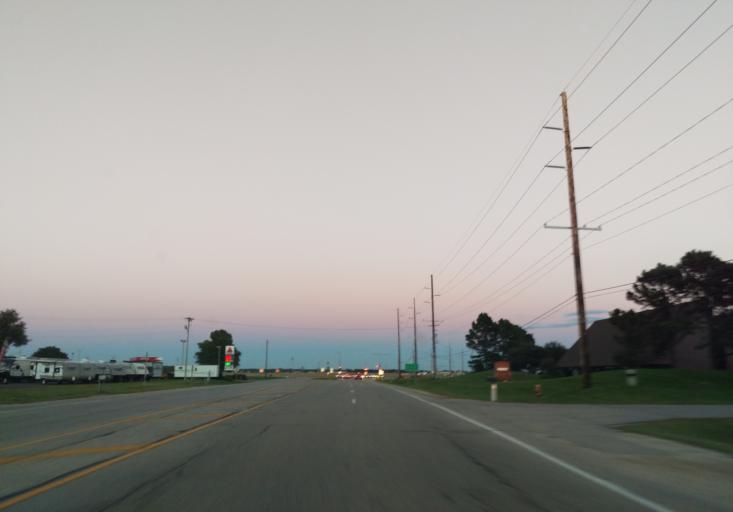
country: US
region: Wisconsin
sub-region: Rock County
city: Janesville
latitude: 42.7306
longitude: -89.0364
